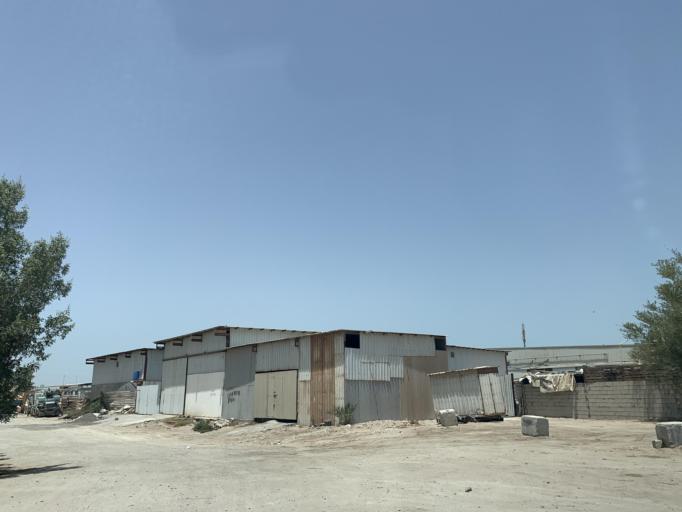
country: BH
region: Northern
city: Sitrah
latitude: 26.1737
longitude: 50.6066
